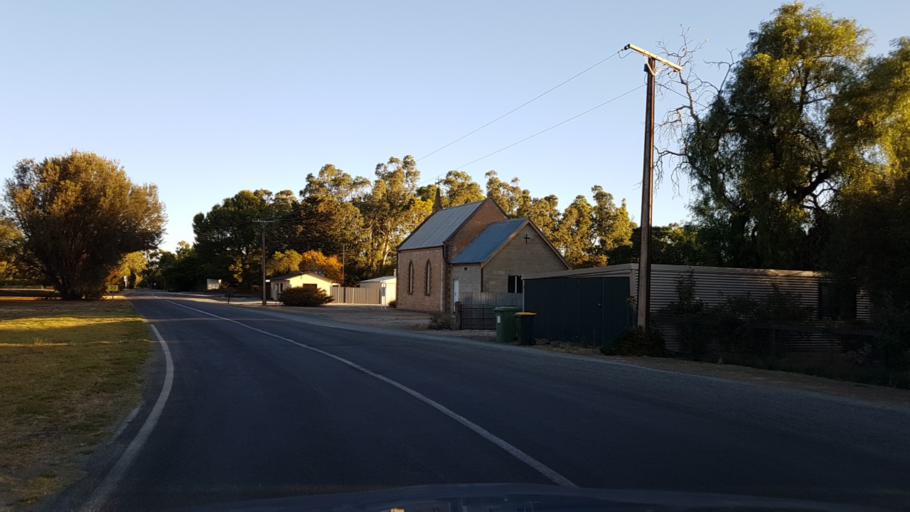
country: AU
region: South Australia
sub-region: Clare and Gilbert Valleys
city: Clare
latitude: -34.0231
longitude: 138.6881
